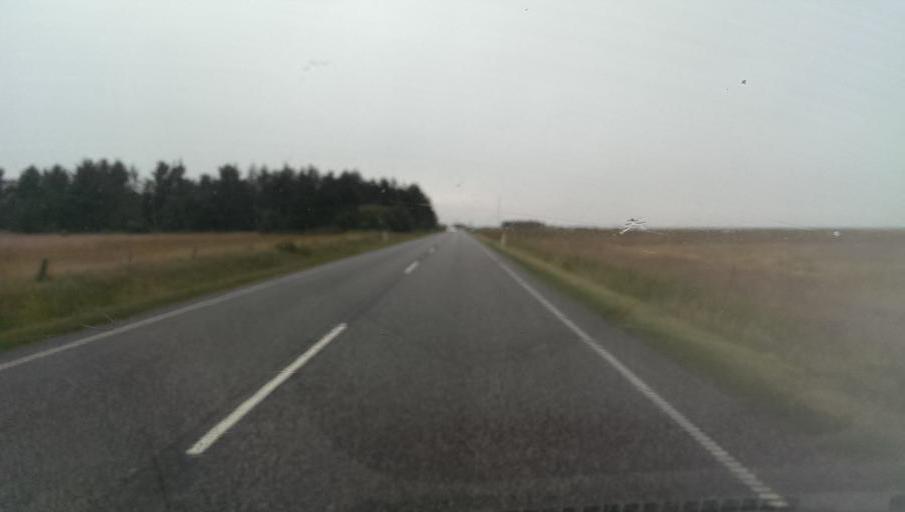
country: DK
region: Central Jutland
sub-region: Ringkobing-Skjern Kommune
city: Hvide Sande
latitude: 55.8584
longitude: 8.1795
